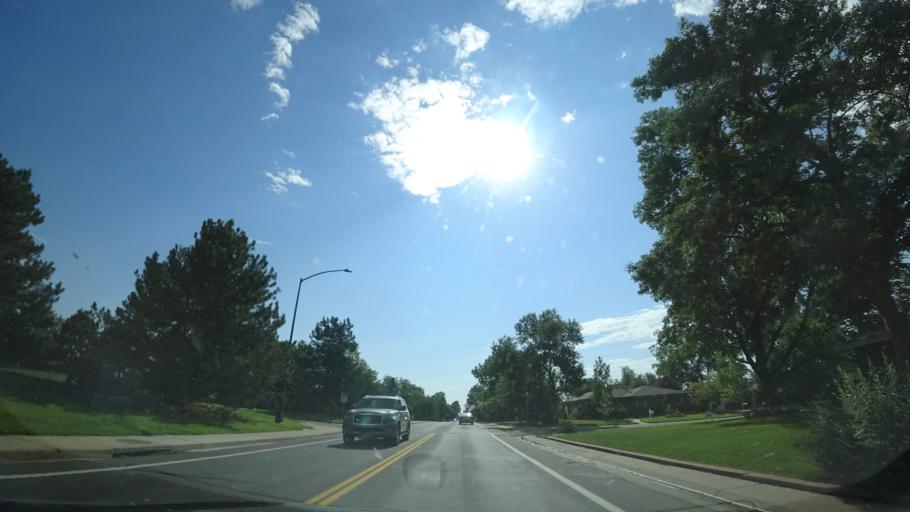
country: US
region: Colorado
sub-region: Jefferson County
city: Lakewood
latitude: 39.7185
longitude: -105.0747
